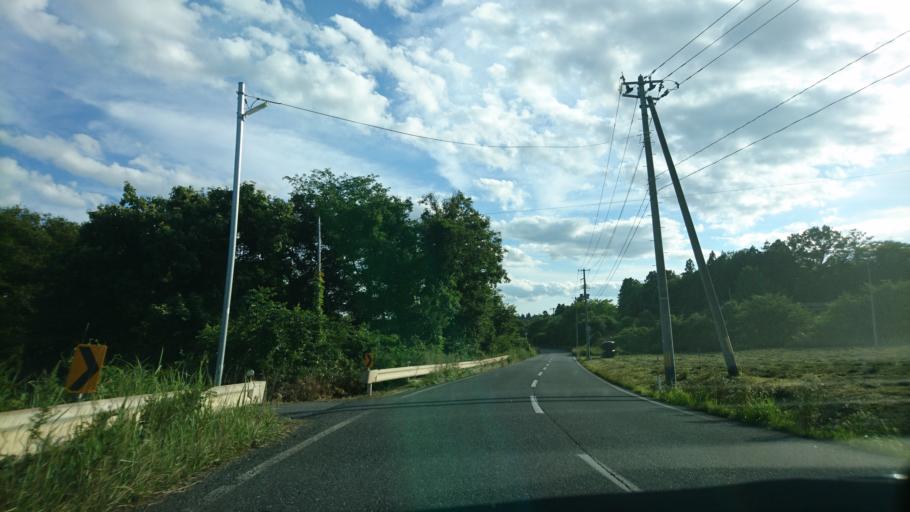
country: JP
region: Iwate
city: Ichinoseki
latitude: 38.8763
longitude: 141.1988
